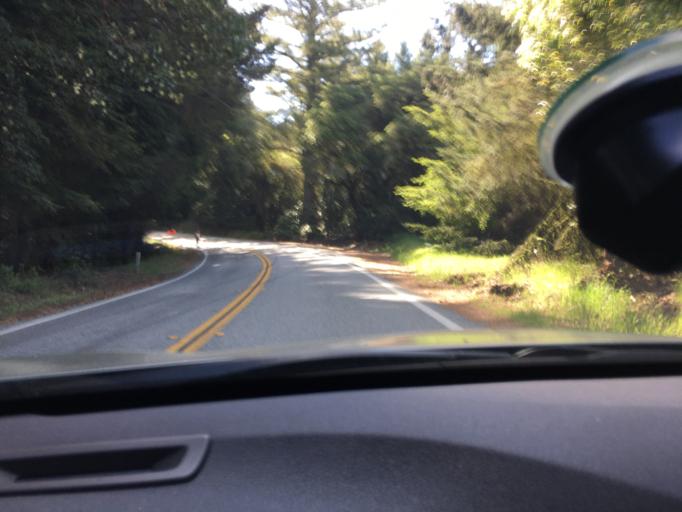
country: US
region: California
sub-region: Santa Clara County
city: Loyola
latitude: 37.2447
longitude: -122.1441
